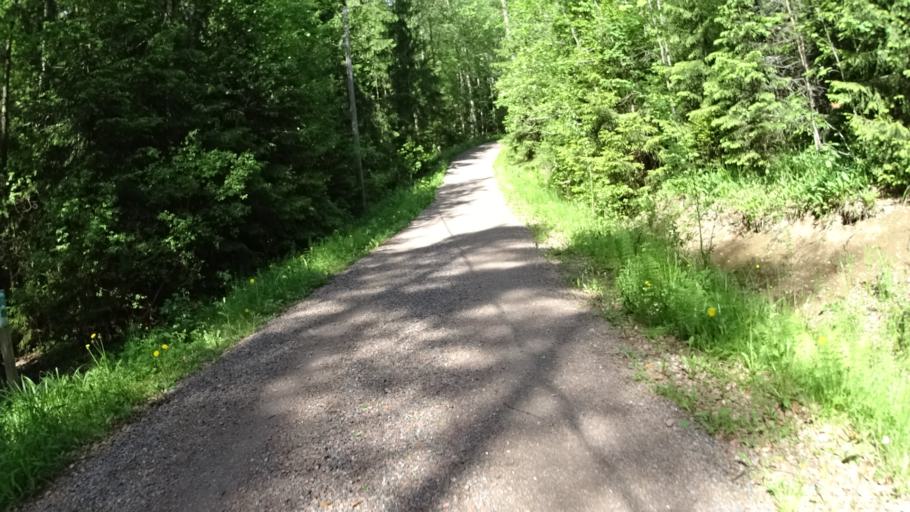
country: FI
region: Uusimaa
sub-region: Helsinki
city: Kauniainen
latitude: 60.3215
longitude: 24.7422
